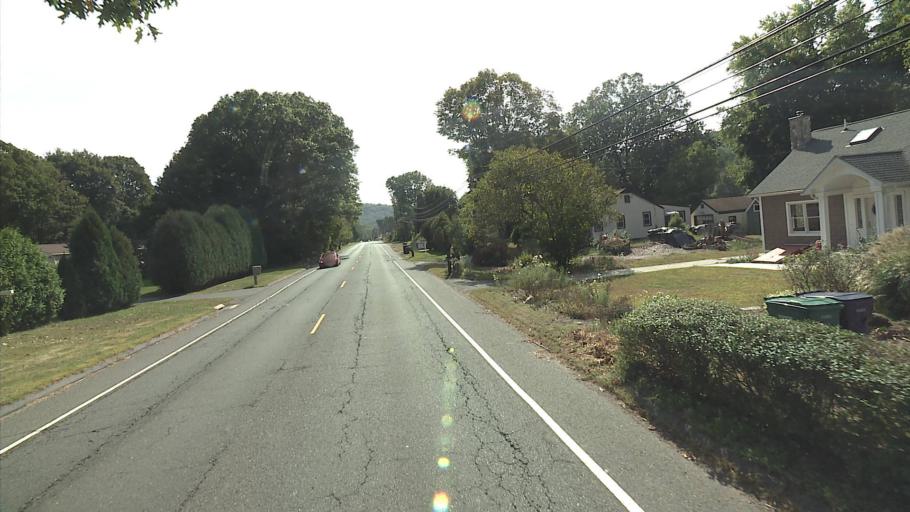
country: US
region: Connecticut
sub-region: New Haven County
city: Oxford
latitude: 41.3700
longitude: -73.1486
